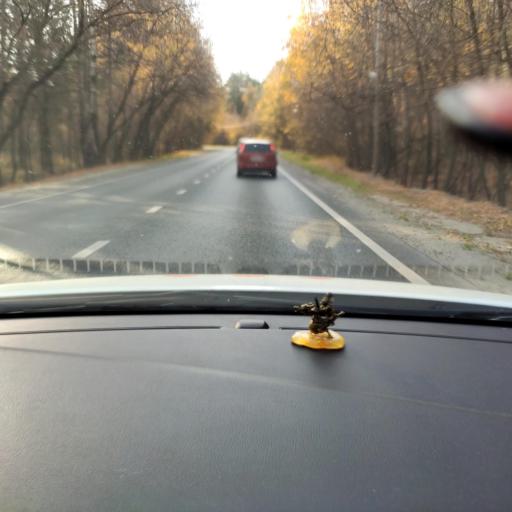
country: RU
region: Tatarstan
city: Osinovo
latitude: 55.8316
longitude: 48.8926
